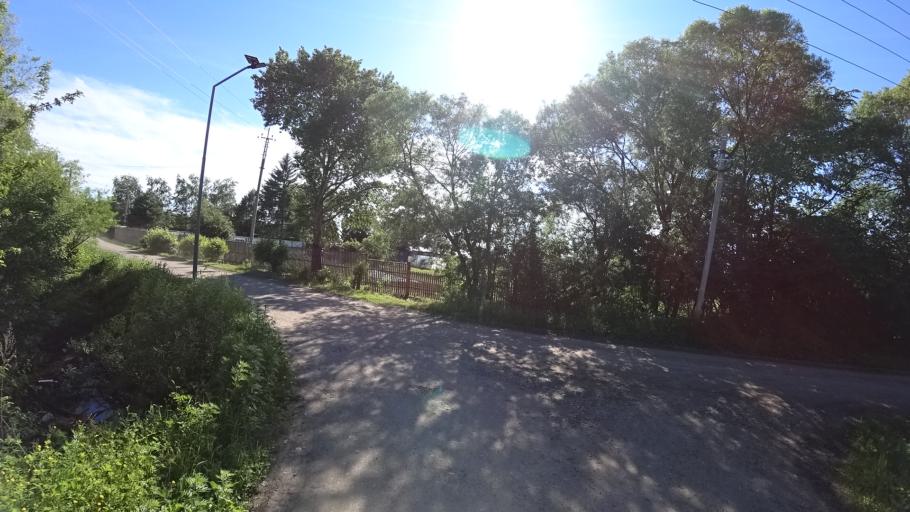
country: RU
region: Khabarovsk Krai
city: Khor
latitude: 47.8878
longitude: 134.9941
